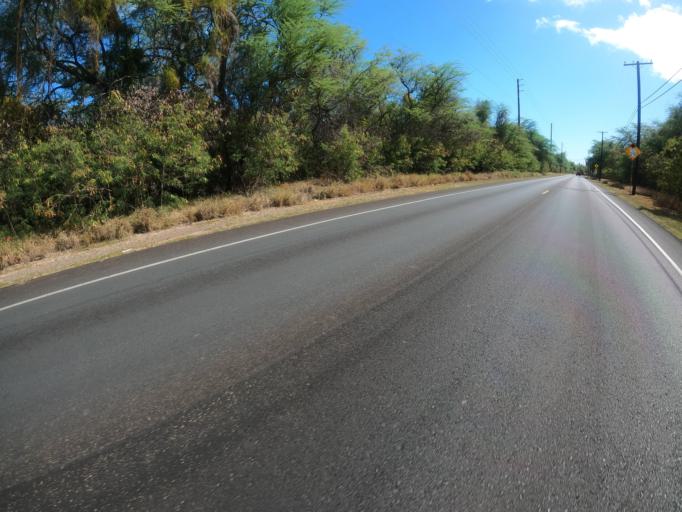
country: US
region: Hawaii
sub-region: Honolulu County
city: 'Ewa Villages
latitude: 21.3068
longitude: -158.0567
